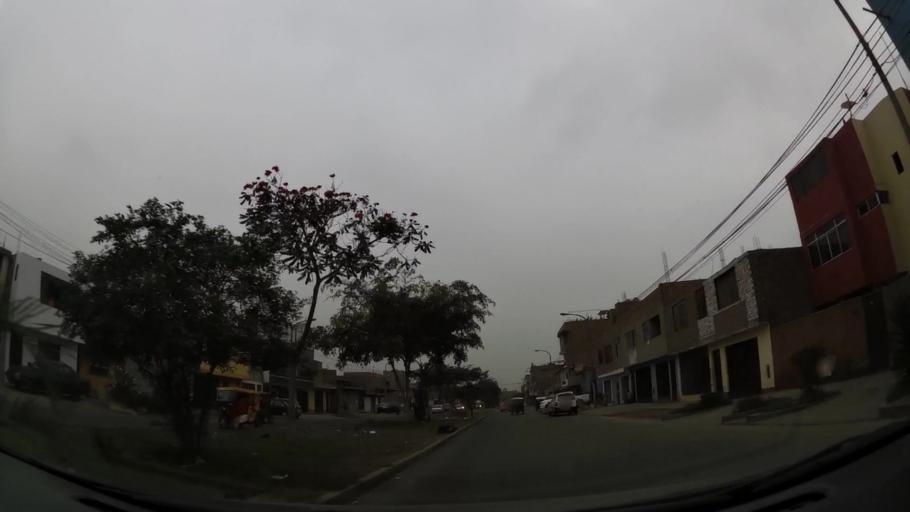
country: PE
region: Lima
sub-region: Lima
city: Urb. Santo Domingo
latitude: -11.9241
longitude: -77.0545
